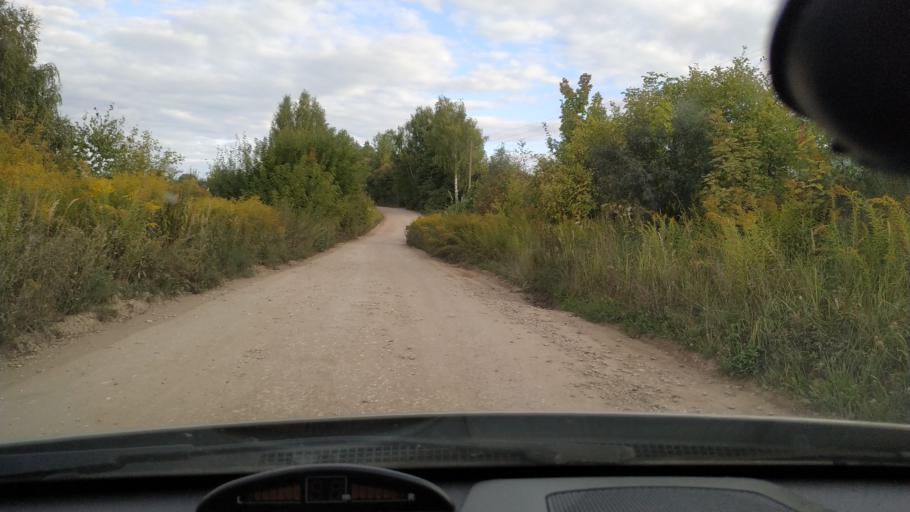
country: RU
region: Rjazan
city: Polyany
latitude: 54.5611
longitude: 39.8758
